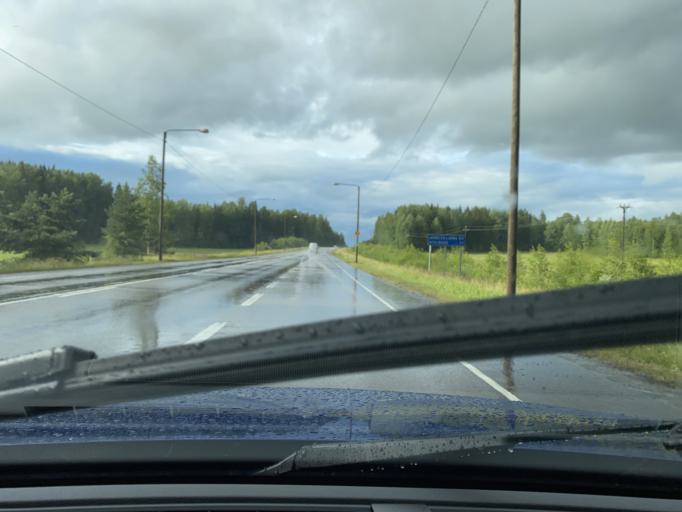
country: FI
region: Uusimaa
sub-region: Helsinki
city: Nurmijaervi
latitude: 60.4602
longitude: 24.8334
